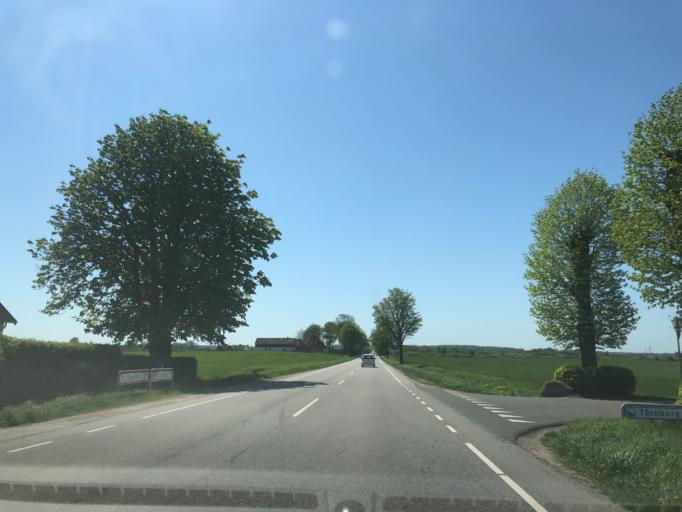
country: DK
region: Zealand
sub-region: Slagelse Kommune
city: Forlev
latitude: 55.3412
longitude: 11.2224
